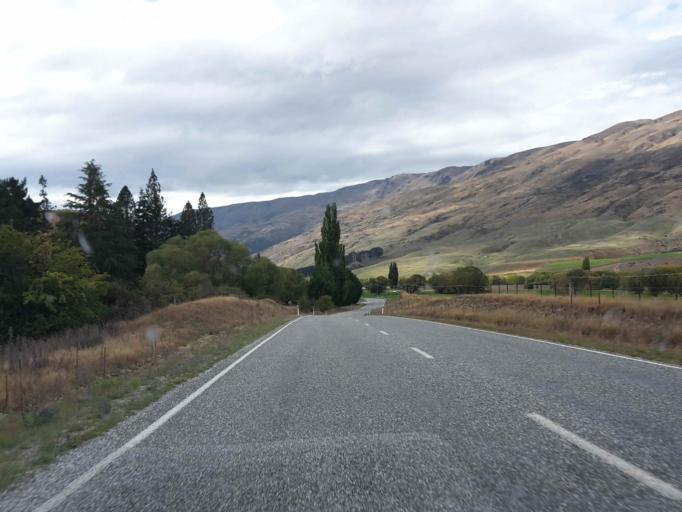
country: NZ
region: Otago
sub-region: Queenstown-Lakes District
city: Wanaka
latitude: -44.8577
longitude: 169.0270
